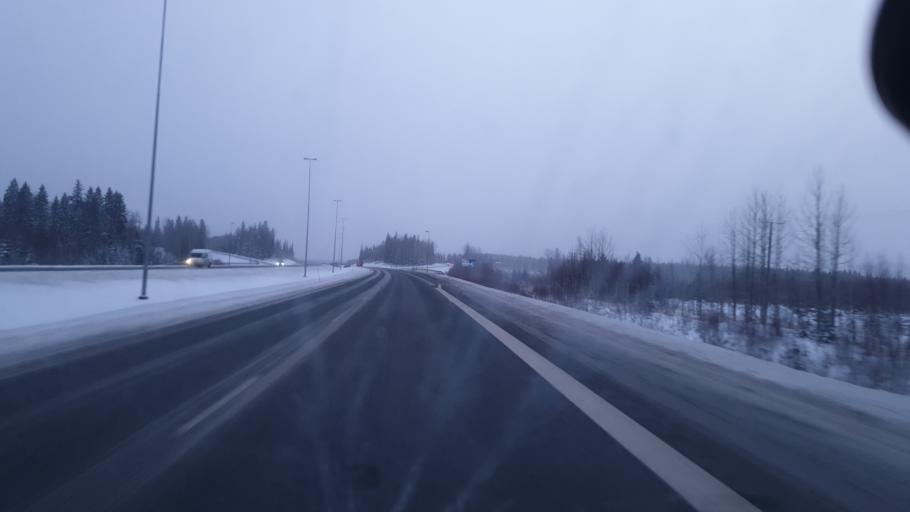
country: FI
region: Lapland
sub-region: Kemi-Tornio
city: Keminmaa
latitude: 65.8259
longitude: 24.3965
